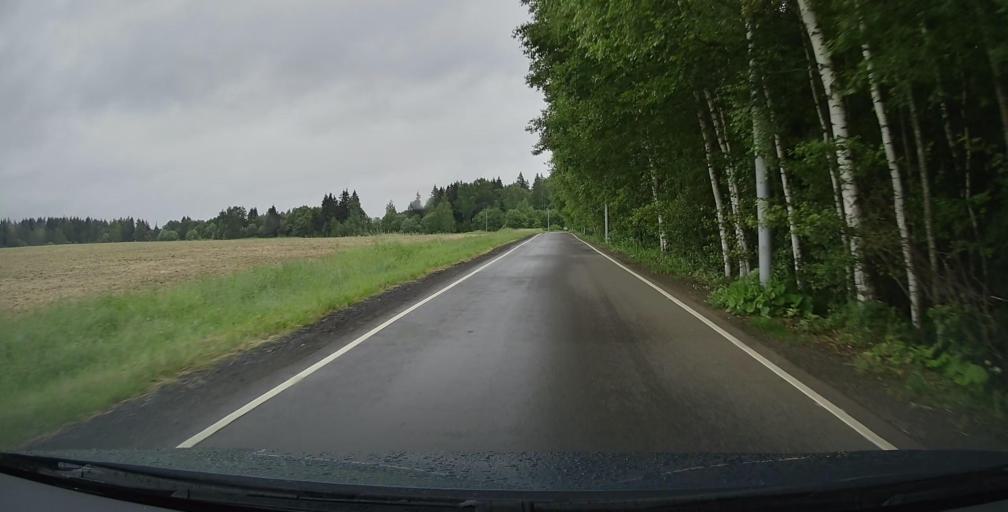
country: RU
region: Moskovskaya
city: Selyatino
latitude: 55.3989
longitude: 37.0140
